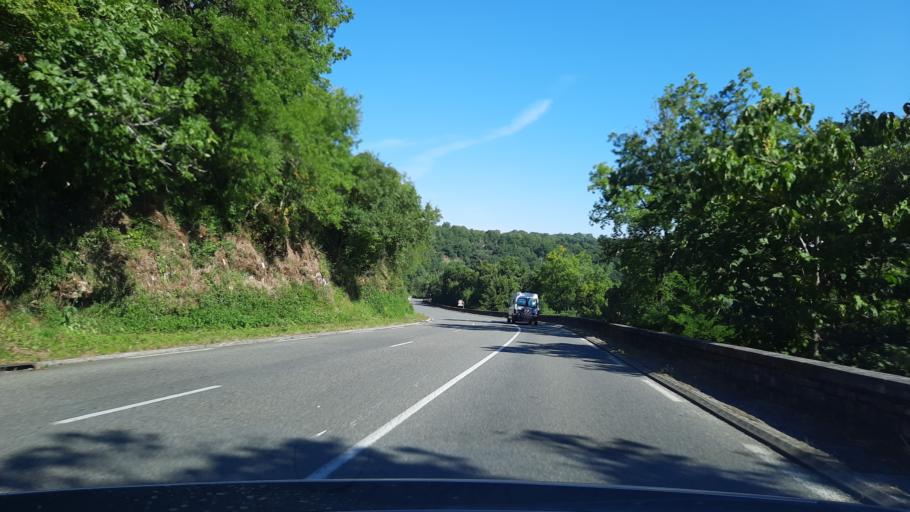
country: FR
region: Midi-Pyrenees
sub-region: Departement du Tarn-et-Garonne
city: Caylus
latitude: 44.2326
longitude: 1.7678
